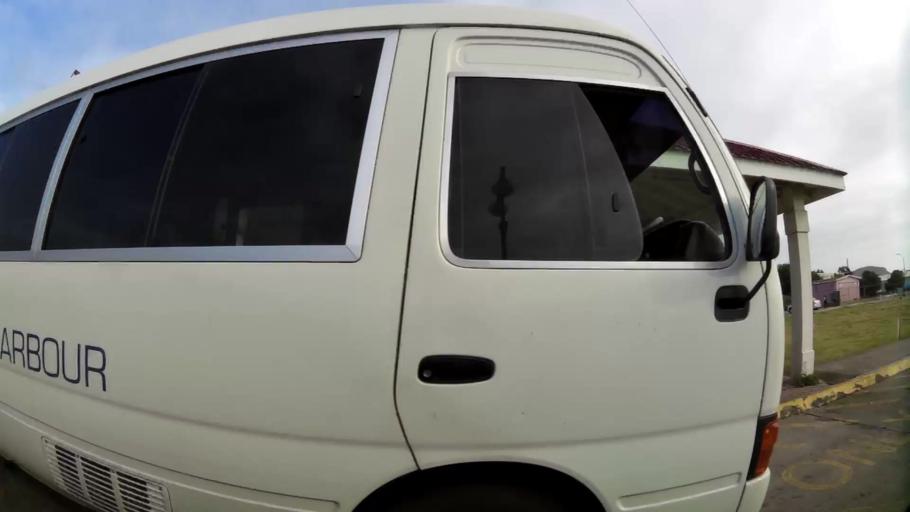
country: KN
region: Saint George Basseterre
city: Basseterre
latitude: 17.2940
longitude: -62.7217
